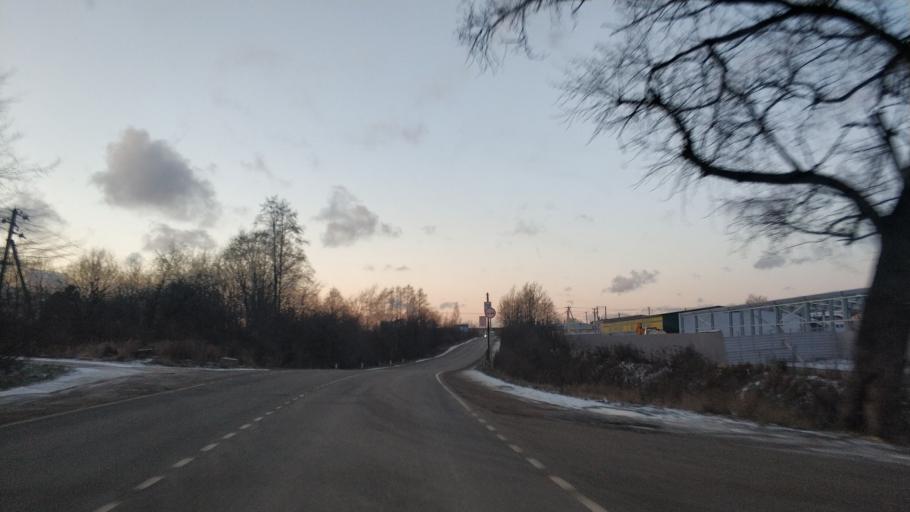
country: RU
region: St.-Petersburg
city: Pontonnyy
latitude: 59.8087
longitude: 30.6149
